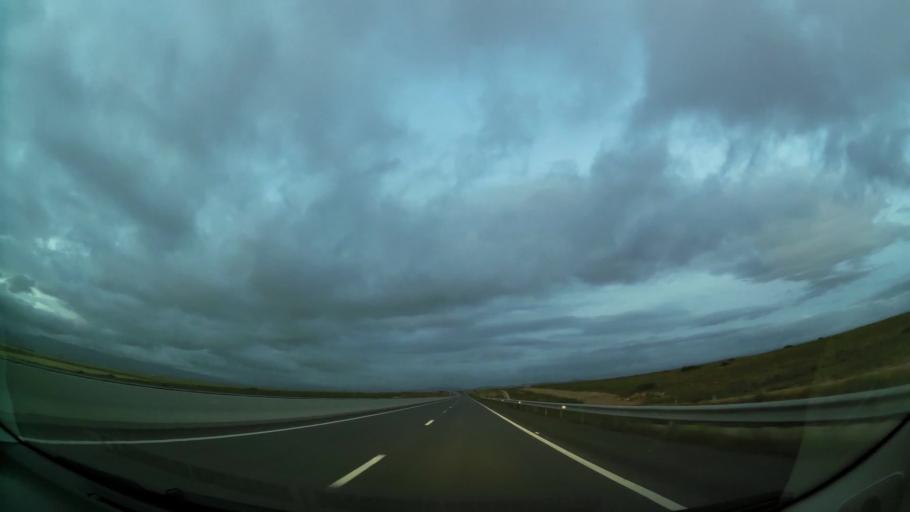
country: MA
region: Oriental
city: El Aioun
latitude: 34.6287
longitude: -2.3640
